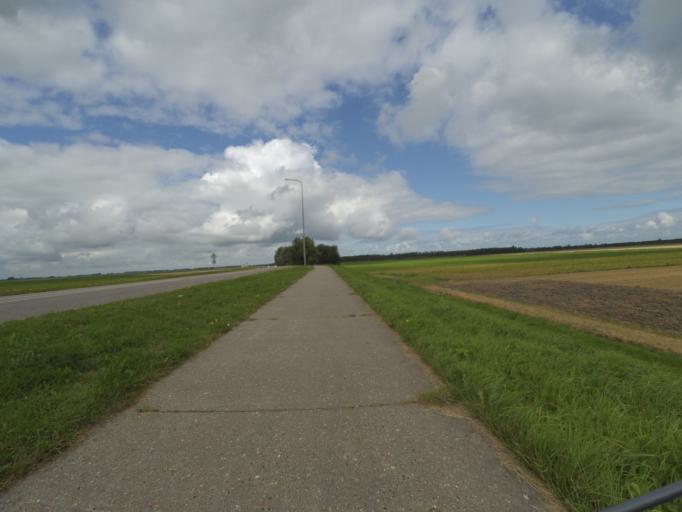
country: NL
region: Groningen
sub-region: Gemeente Zuidhorn
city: Grijpskerk
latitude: 53.3150
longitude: 6.2640
